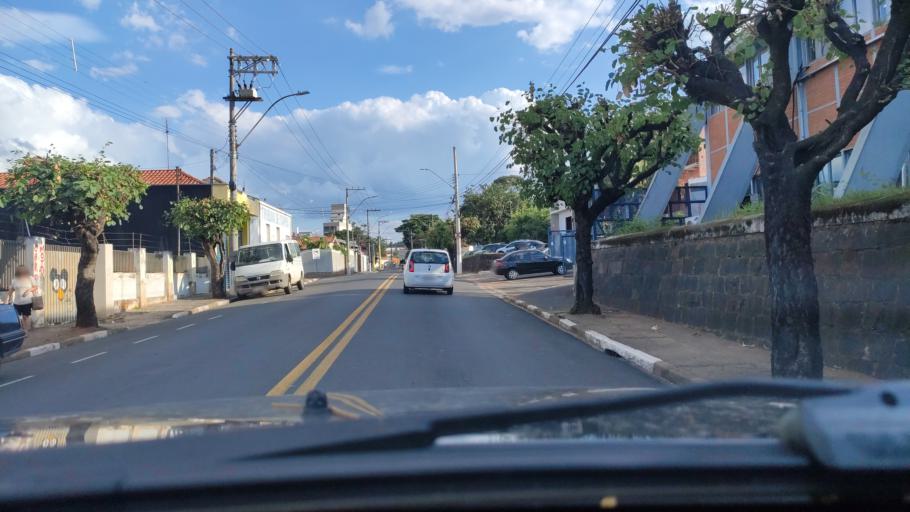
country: BR
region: Sao Paulo
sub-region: Itapira
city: Itapira
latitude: -22.4354
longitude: -46.8251
